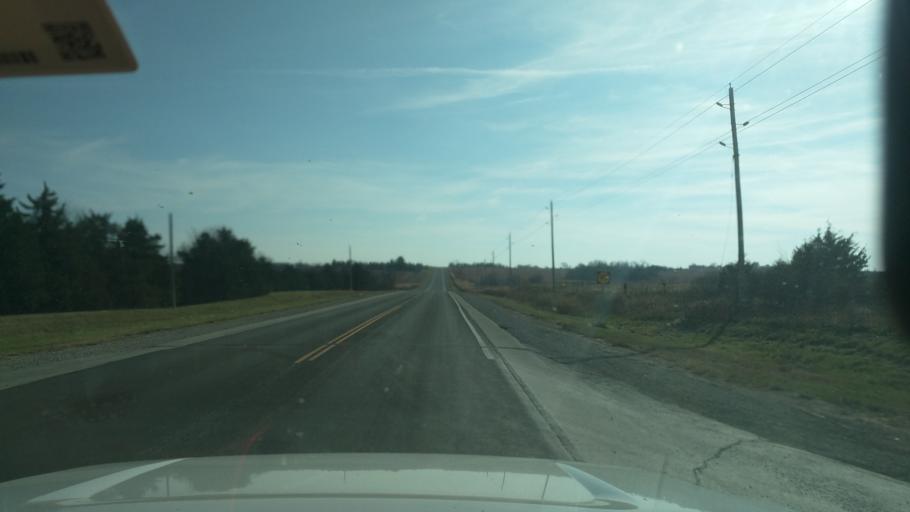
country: US
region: Kansas
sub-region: Lyon County
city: Emporia
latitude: 38.3469
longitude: -96.1803
